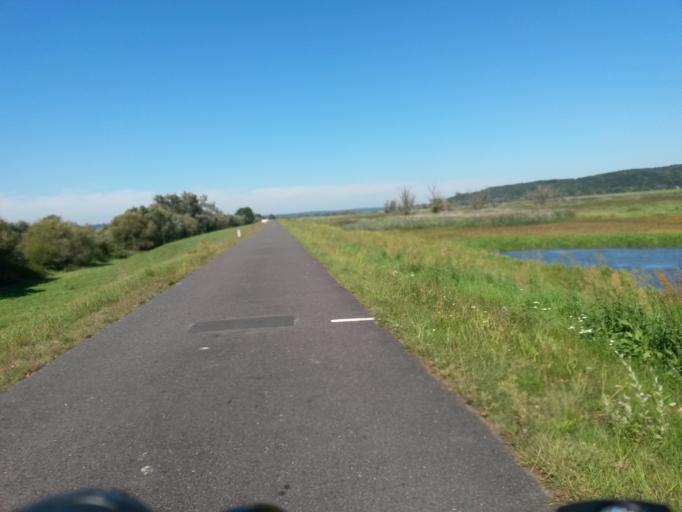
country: PL
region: West Pomeranian Voivodeship
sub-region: Powiat gryfinski
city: Cedynia
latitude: 52.9157
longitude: 14.1439
